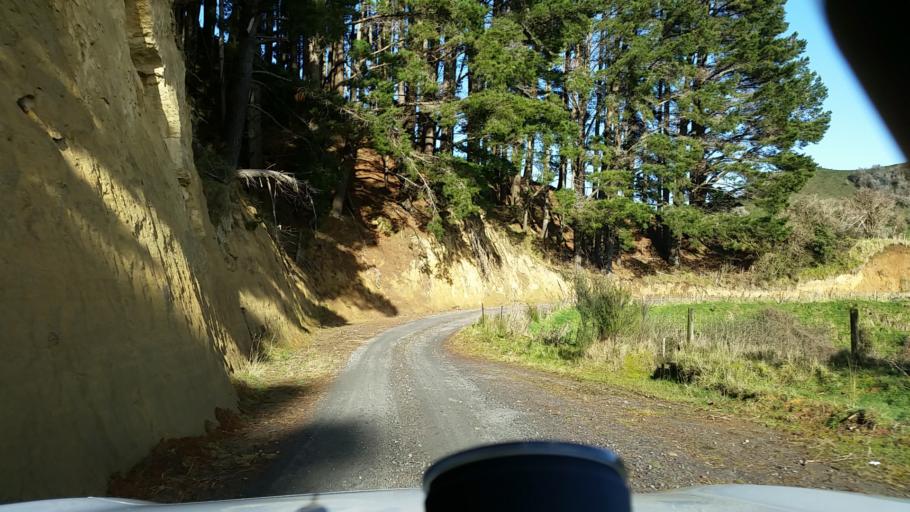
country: NZ
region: Taranaki
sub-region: South Taranaki District
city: Eltham
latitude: -39.4095
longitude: 174.5344
